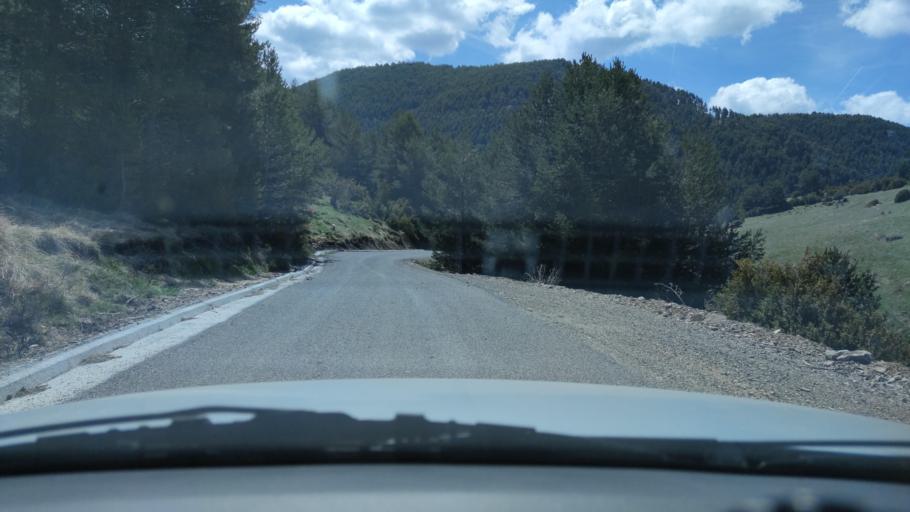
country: ES
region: Catalonia
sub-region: Provincia de Lleida
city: Sort
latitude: 42.3125
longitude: 1.1627
